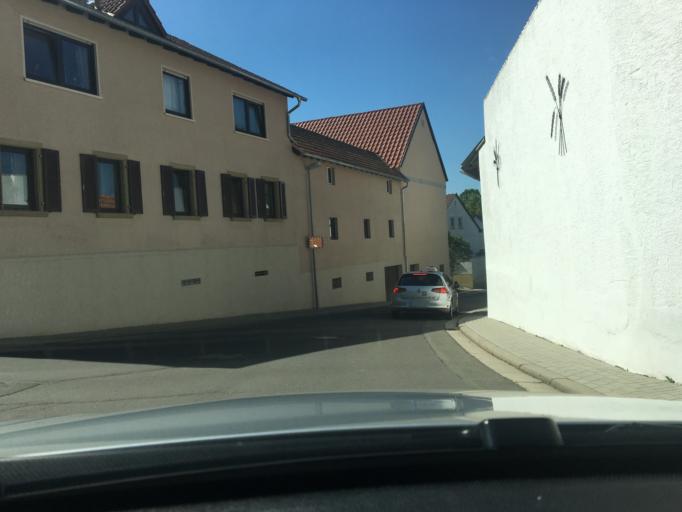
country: DE
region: Rheinland-Pfalz
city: Mauchenheim
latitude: 49.7180
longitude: 8.0450
